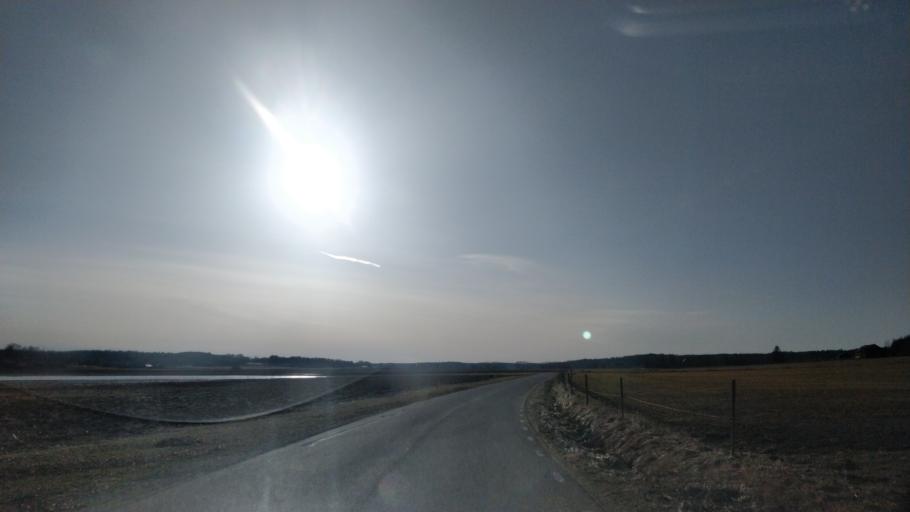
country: SE
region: Uppsala
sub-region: Enkopings Kommun
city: Orsundsbro
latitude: 59.7470
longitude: 17.1957
